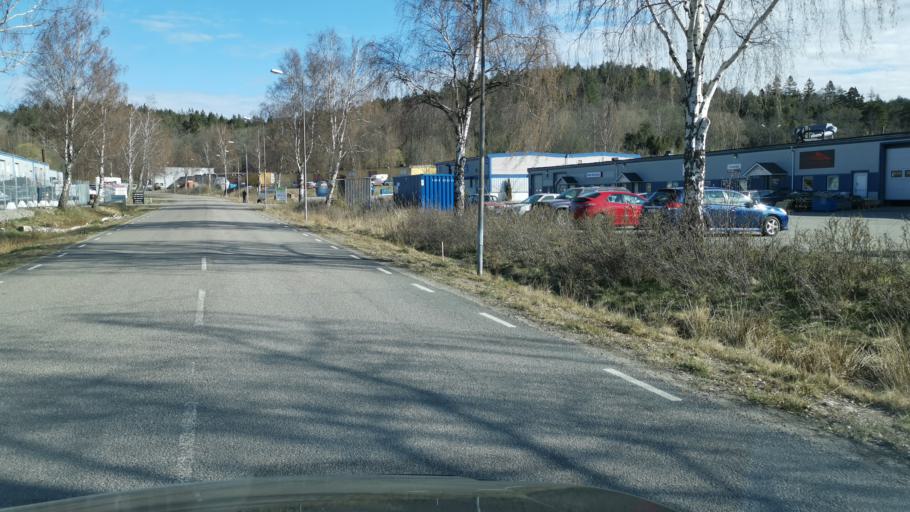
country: SE
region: Vaestra Goetaland
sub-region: Uddevalla Kommun
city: Uddevalla
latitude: 58.3570
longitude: 11.9767
